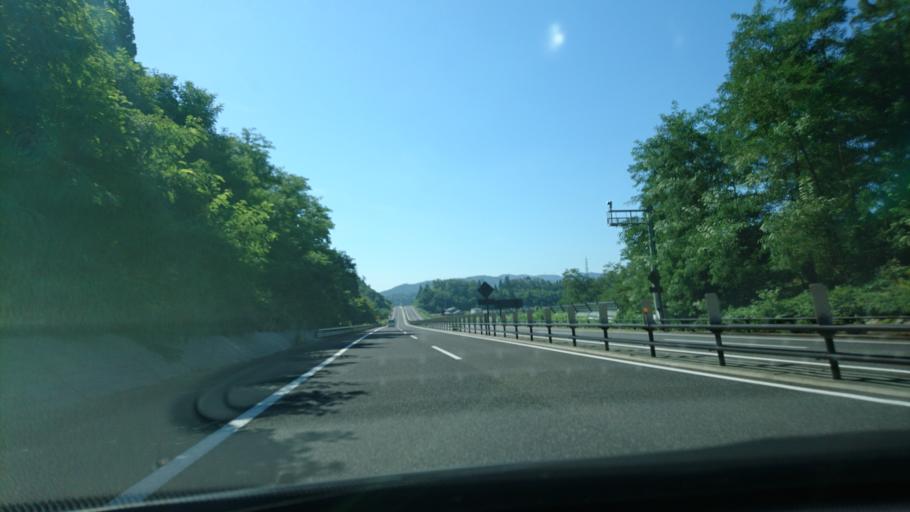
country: JP
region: Iwate
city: Hanamaki
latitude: 39.3577
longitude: 141.2382
